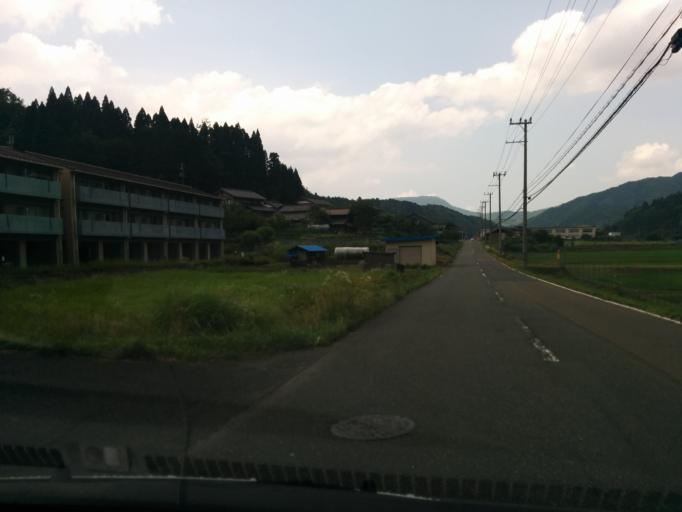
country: JP
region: Kyoto
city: Fukuchiyama
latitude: 35.4060
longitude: 135.1506
